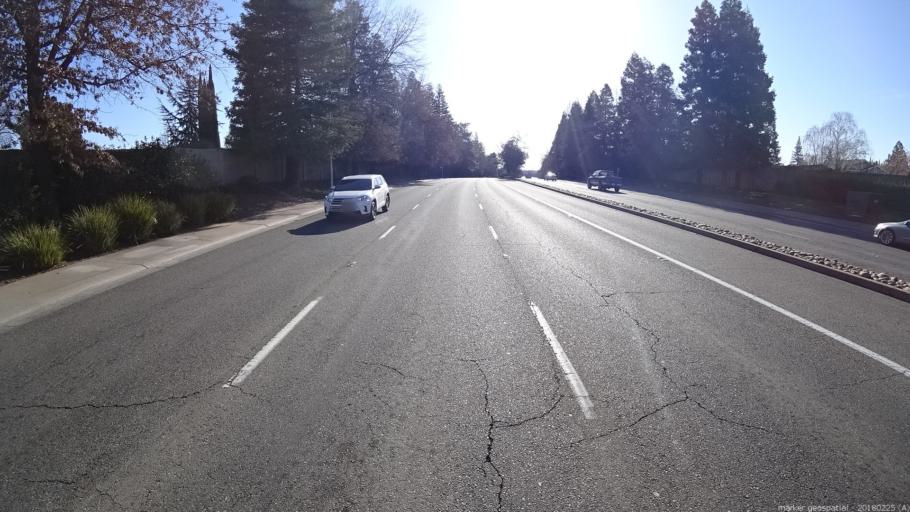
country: US
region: California
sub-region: Sacramento County
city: North Highlands
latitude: 38.7182
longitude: -121.3773
